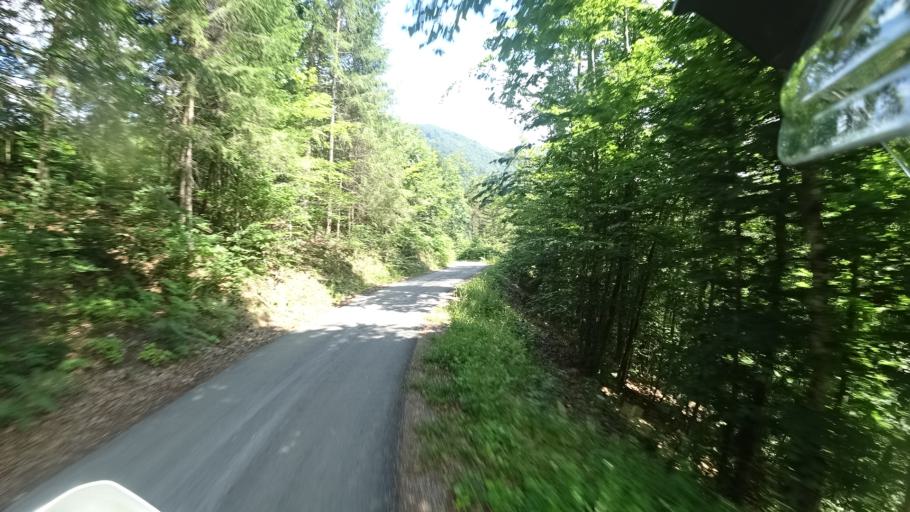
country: SI
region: Osilnica
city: Osilnica
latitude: 45.5104
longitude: 14.6946
